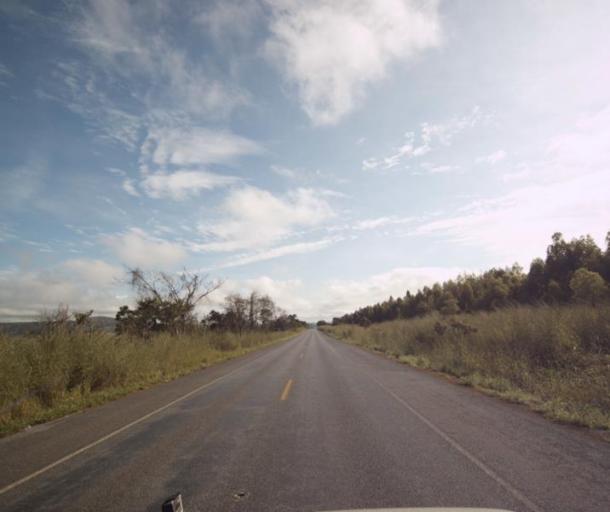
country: BR
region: Goias
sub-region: Pirenopolis
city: Pirenopolis
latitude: -15.5101
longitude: -48.6220
